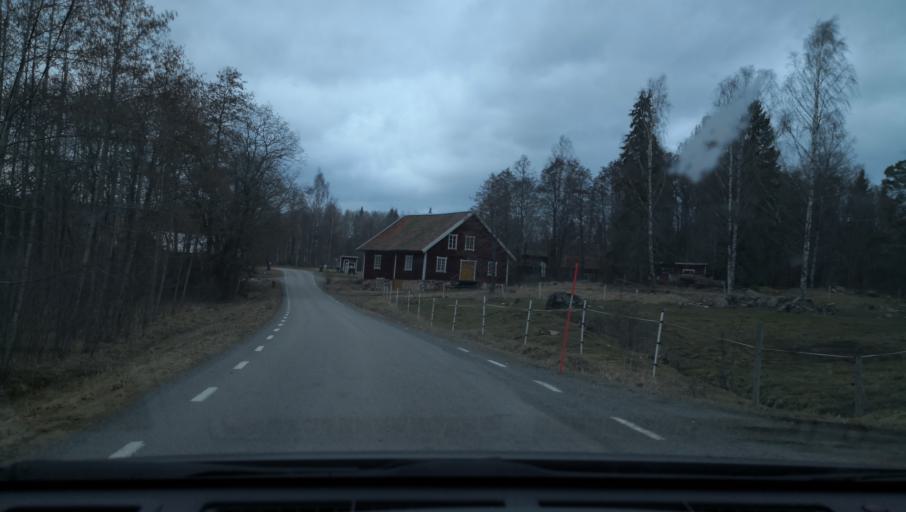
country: SE
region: Vaestmanland
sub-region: Kopings Kommun
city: Kolsva
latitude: 59.5678
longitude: 15.7311
